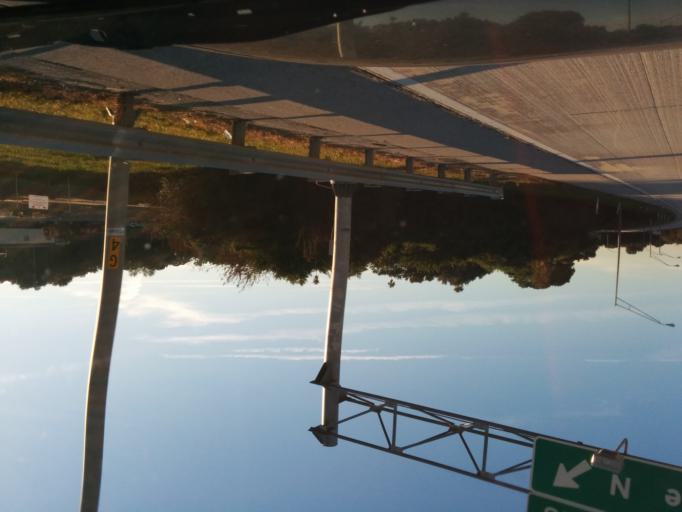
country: US
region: Florida
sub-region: Pinellas County
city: Lealman
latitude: 27.8258
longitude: -82.6662
